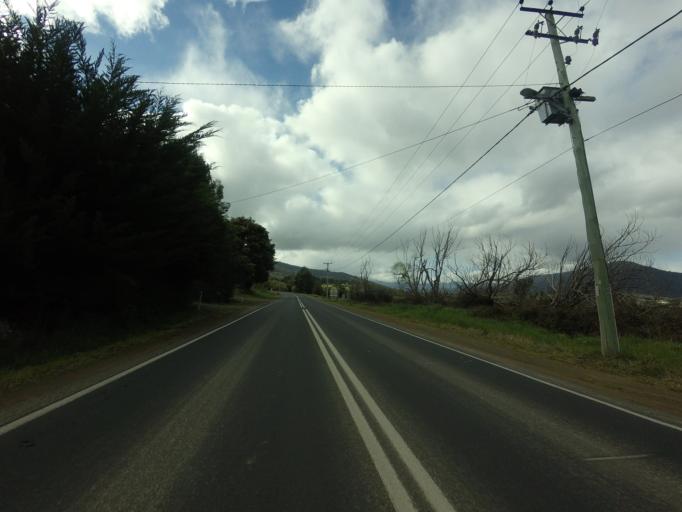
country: AU
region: Tasmania
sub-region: Huon Valley
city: Franklin
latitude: -43.0792
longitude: 147.0172
